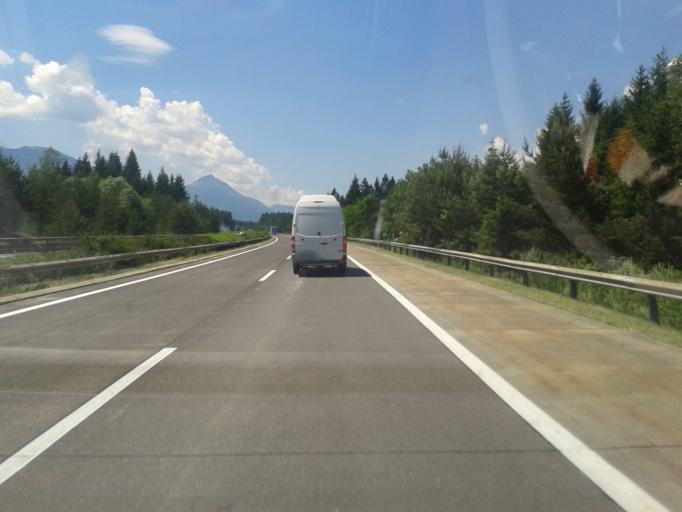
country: AT
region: Carinthia
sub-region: Politischer Bezirk Villach Land
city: Arnoldstein
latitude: 46.5682
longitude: 13.7269
